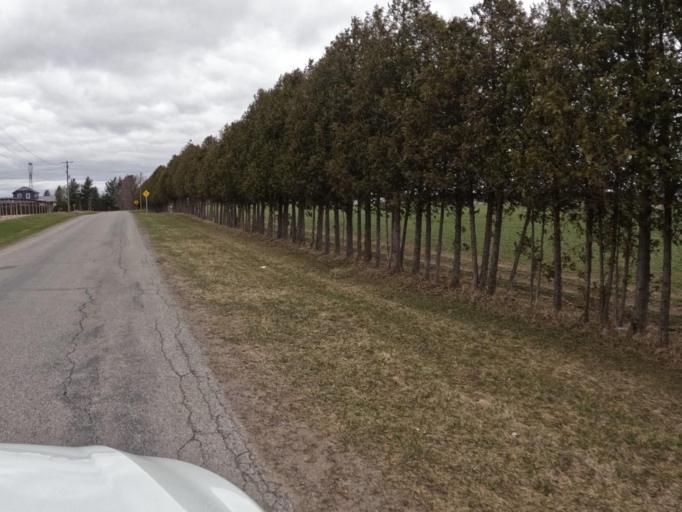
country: CA
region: Ontario
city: Norfolk County
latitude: 42.9600
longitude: -80.3962
